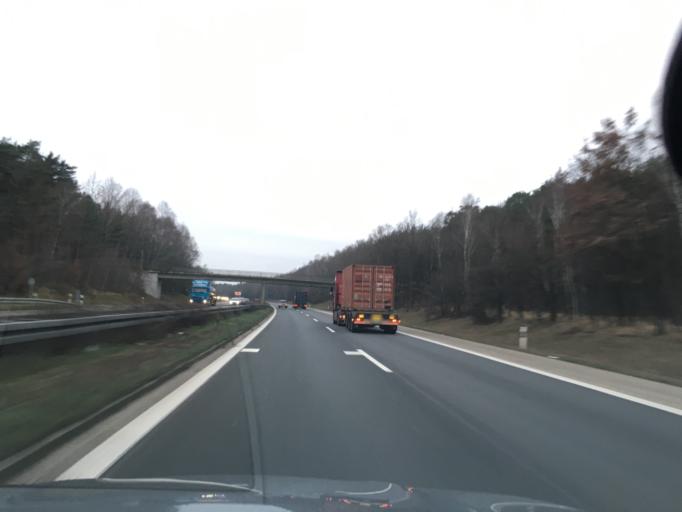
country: DE
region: Bavaria
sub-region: Regierungsbezirk Mittelfranken
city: Hochstadt an der Aisch
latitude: 49.7354
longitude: 10.8072
